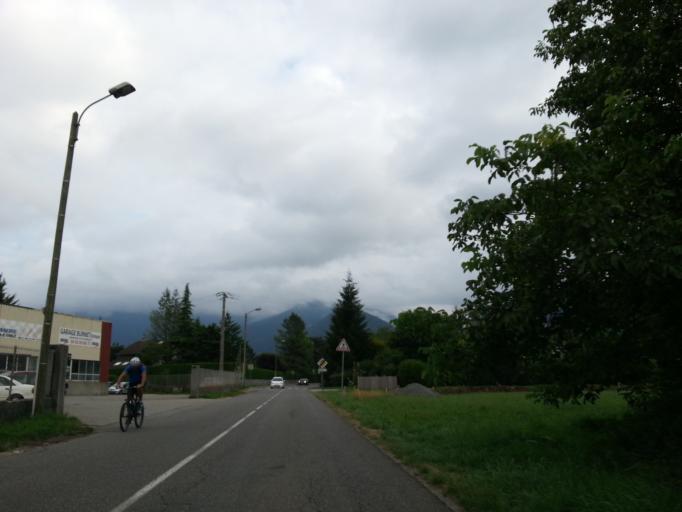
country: FR
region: Rhone-Alpes
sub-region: Departement de la Haute-Savoie
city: Doussard
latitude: 45.7849
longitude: 6.2306
